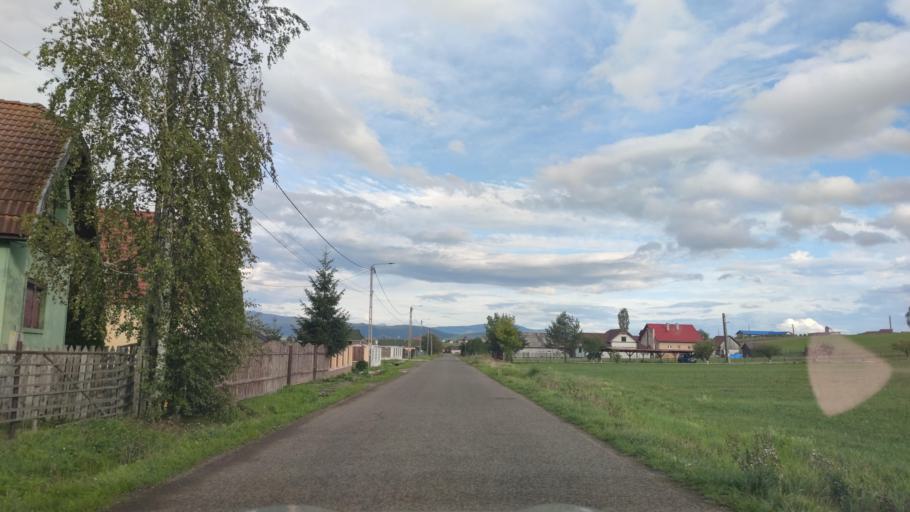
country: RO
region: Harghita
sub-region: Comuna Remetea
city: Remetea
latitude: 46.8026
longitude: 25.4365
